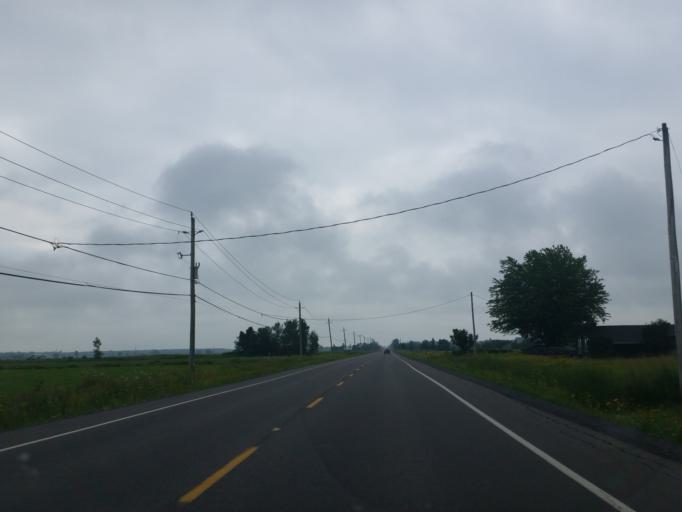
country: CA
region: Ontario
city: Clarence-Rockland
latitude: 45.4534
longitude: -75.4446
